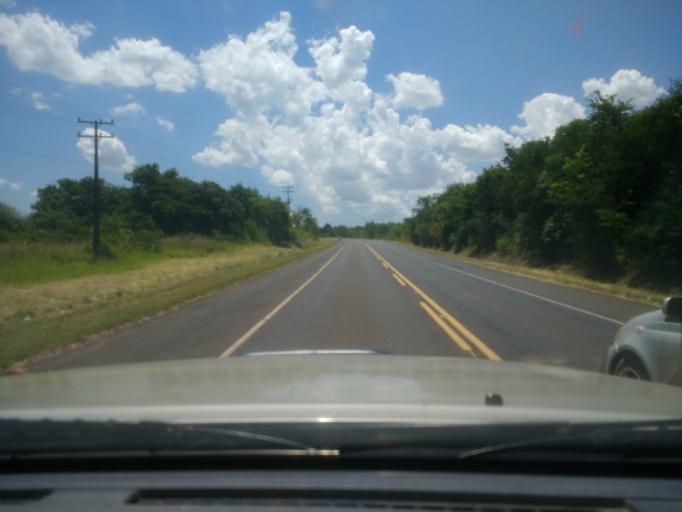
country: PY
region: San Pedro
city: Guayaybi
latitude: -24.5999
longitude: -56.5032
